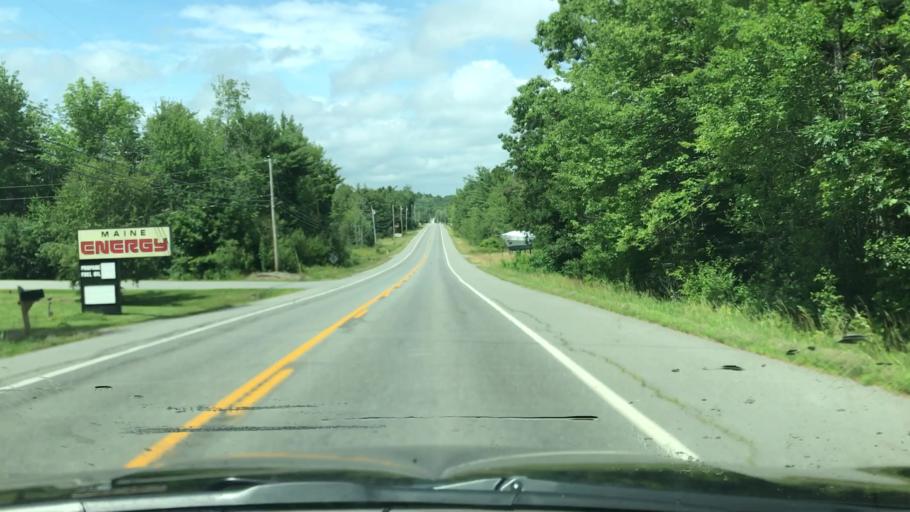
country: US
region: Maine
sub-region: Waldo County
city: Northport
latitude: 44.3745
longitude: -68.9843
